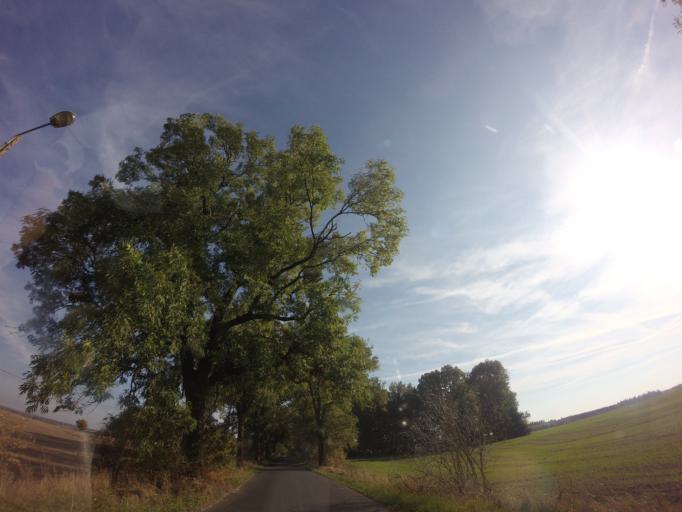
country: PL
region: West Pomeranian Voivodeship
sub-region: Powiat choszczenski
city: Recz
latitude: 53.2166
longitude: 15.6114
